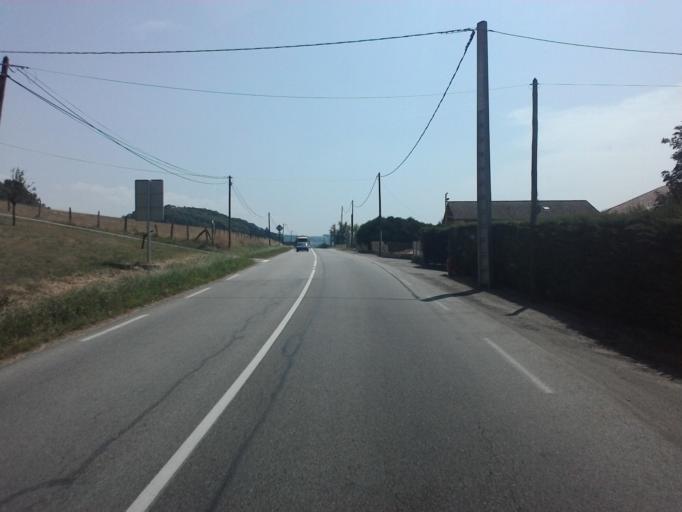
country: FR
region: Rhone-Alpes
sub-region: Departement de l'Isere
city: Montferrat
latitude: 45.5071
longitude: 5.5943
